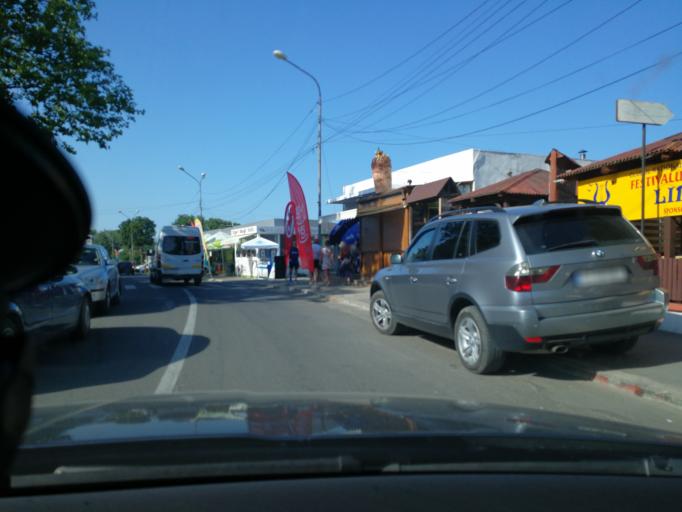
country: RO
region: Constanta
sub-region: Municipiul Mangalia
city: Mangalia
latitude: 43.8470
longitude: 28.5994
